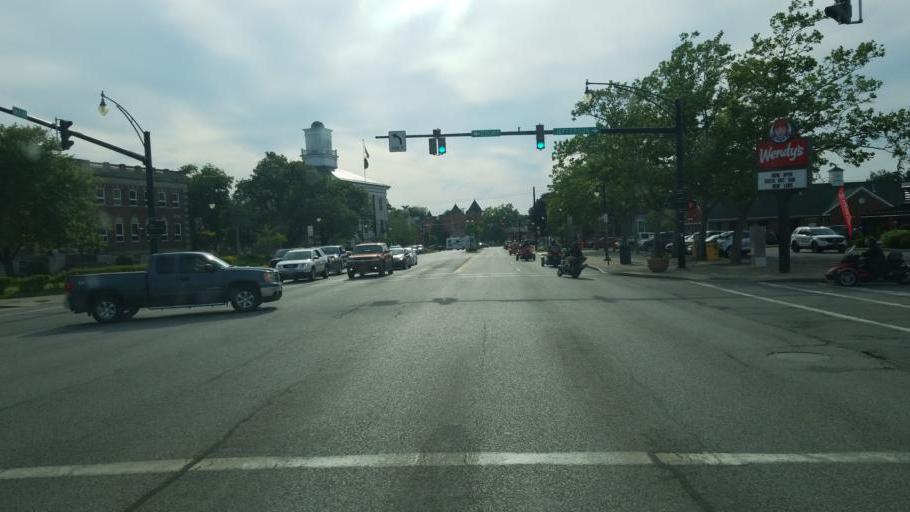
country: US
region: New York
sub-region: Genesee County
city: Batavia
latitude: 42.9978
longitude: -78.1852
